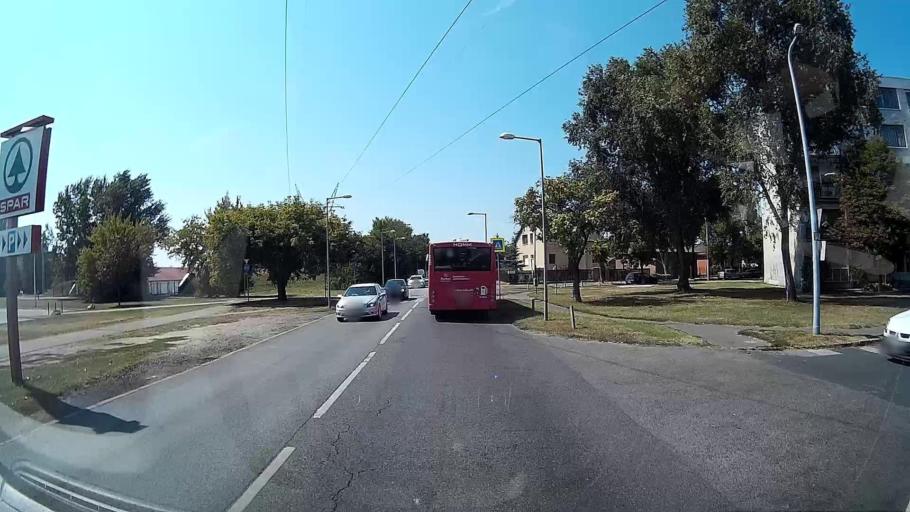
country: HU
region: Budapest
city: Budapest XVIII. keruelet
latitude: 47.4318
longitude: 19.1724
